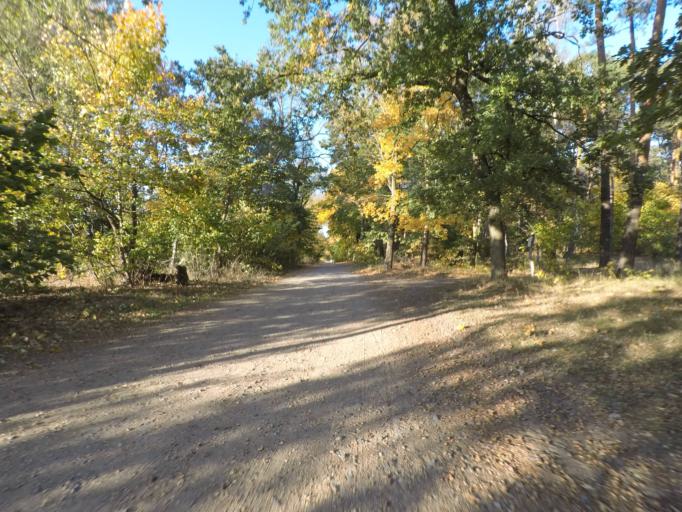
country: DE
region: Brandenburg
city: Biesenthal
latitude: 52.7751
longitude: 13.6416
